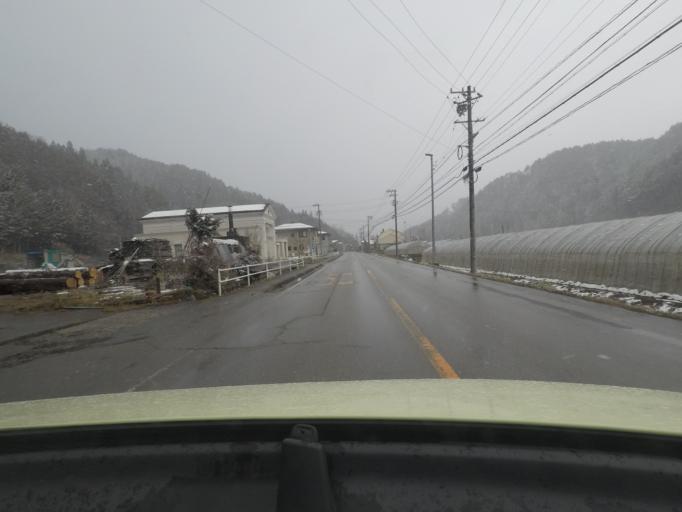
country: JP
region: Gifu
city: Takayama
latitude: 36.1489
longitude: 137.2860
